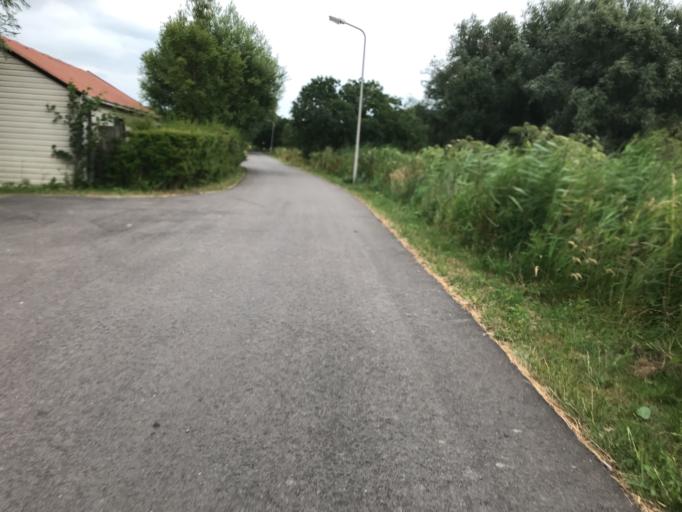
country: NL
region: North Holland
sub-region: Gemeente Diemen
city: Diemen
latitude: 52.3366
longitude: 4.9824
